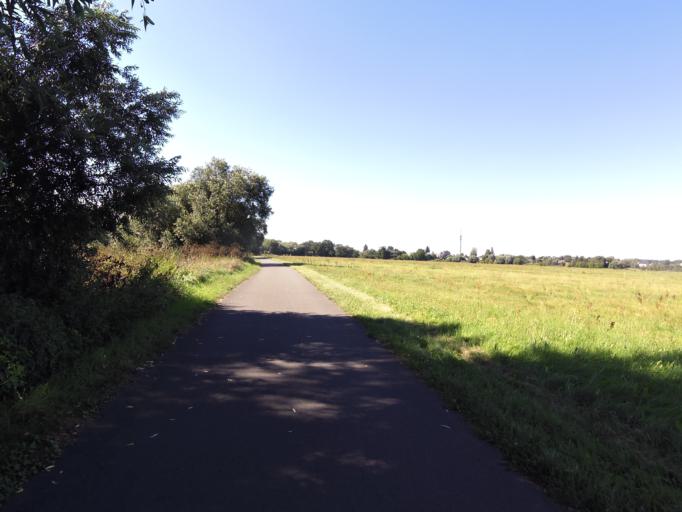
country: DE
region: Saxony-Anhalt
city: Abtsdorf
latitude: 51.8582
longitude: 12.6877
